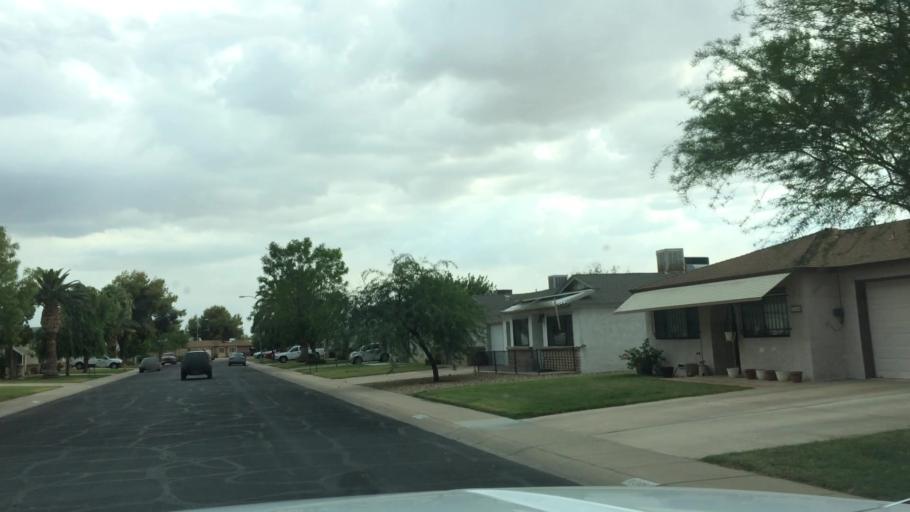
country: US
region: Arizona
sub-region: Maricopa County
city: Sun City
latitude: 33.5783
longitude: -112.2665
